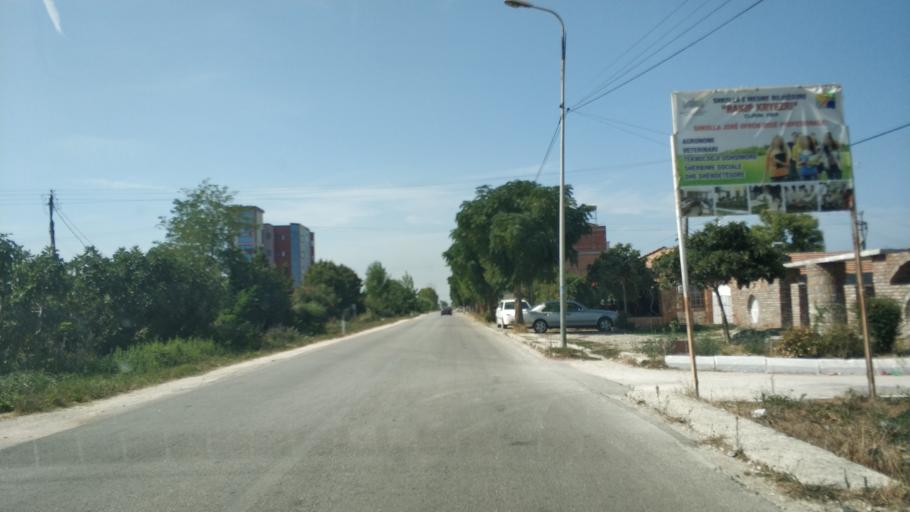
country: AL
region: Fier
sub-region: Rrethi i Fierit
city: Dermenas
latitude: 40.7356
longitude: 19.5245
